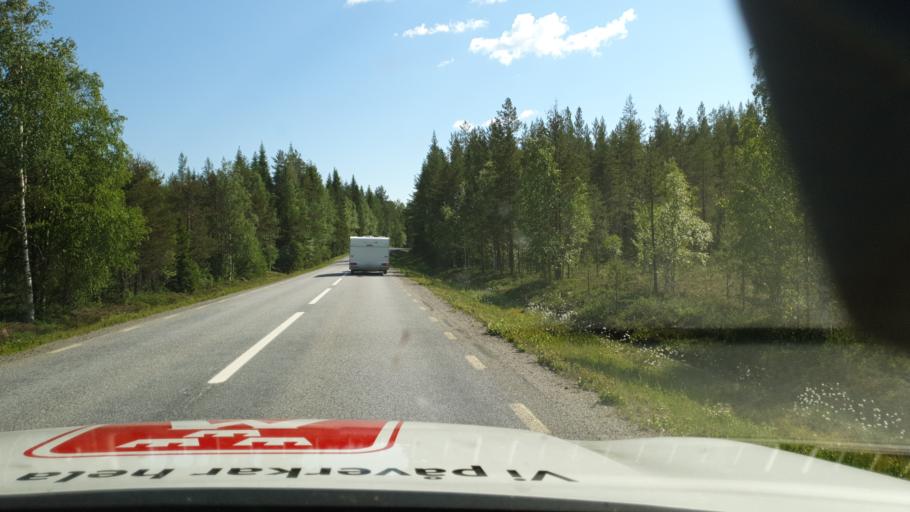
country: SE
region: Vaesterbotten
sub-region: Skelleftea Kommun
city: Burtraesk
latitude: 64.3426
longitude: 20.2333
